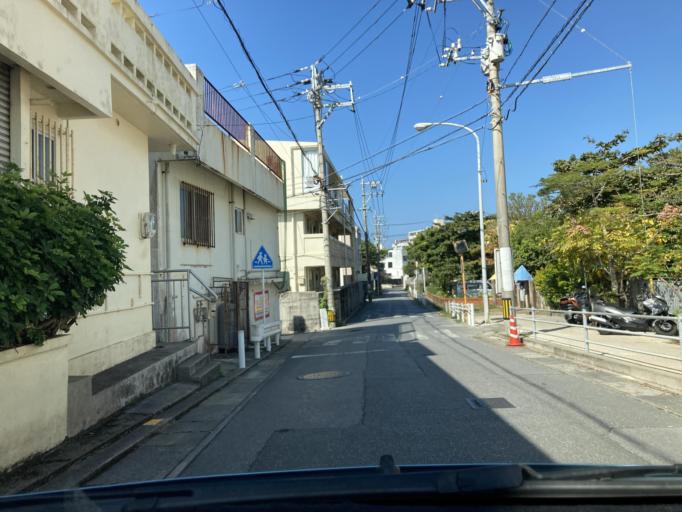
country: JP
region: Okinawa
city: Naha-shi
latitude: 26.2267
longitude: 127.7220
